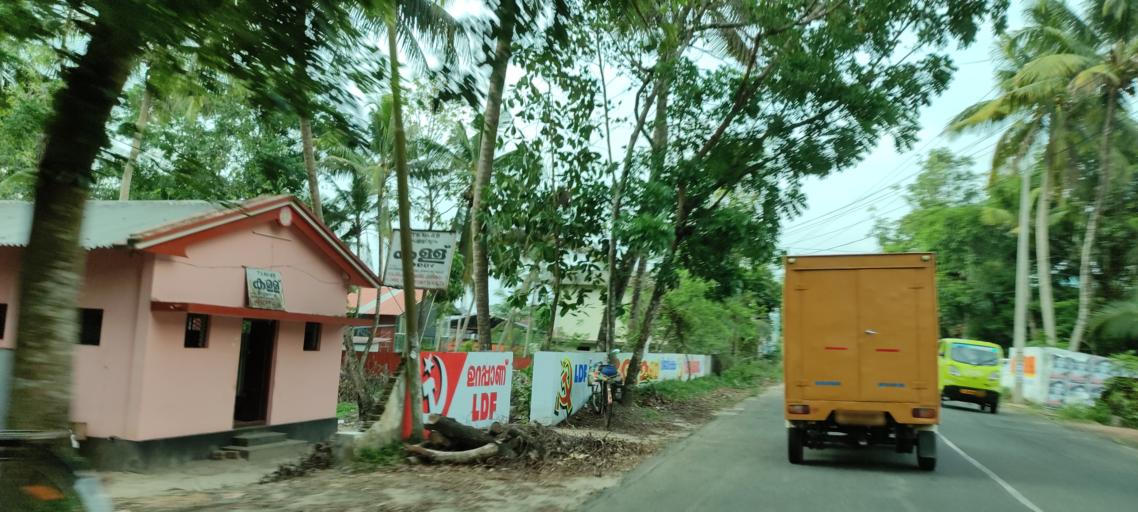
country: IN
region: Kerala
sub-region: Kottayam
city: Vaikam
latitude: 9.7518
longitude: 76.3632
